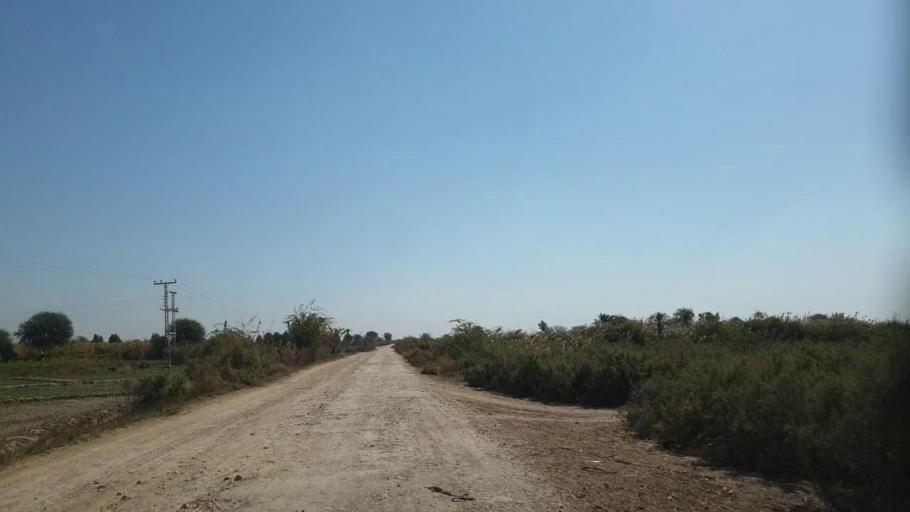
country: PK
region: Sindh
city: Mirpur Khas
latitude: 25.5914
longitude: 69.1029
